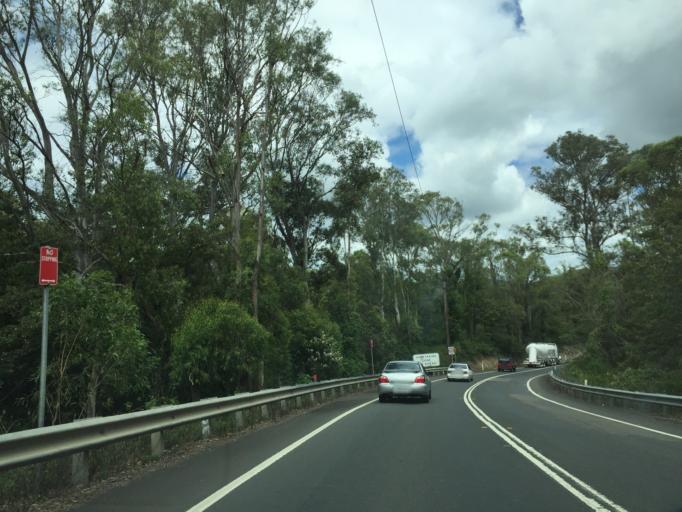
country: AU
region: New South Wales
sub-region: Hawkesbury
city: Richmond
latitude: -33.5492
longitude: 150.6735
